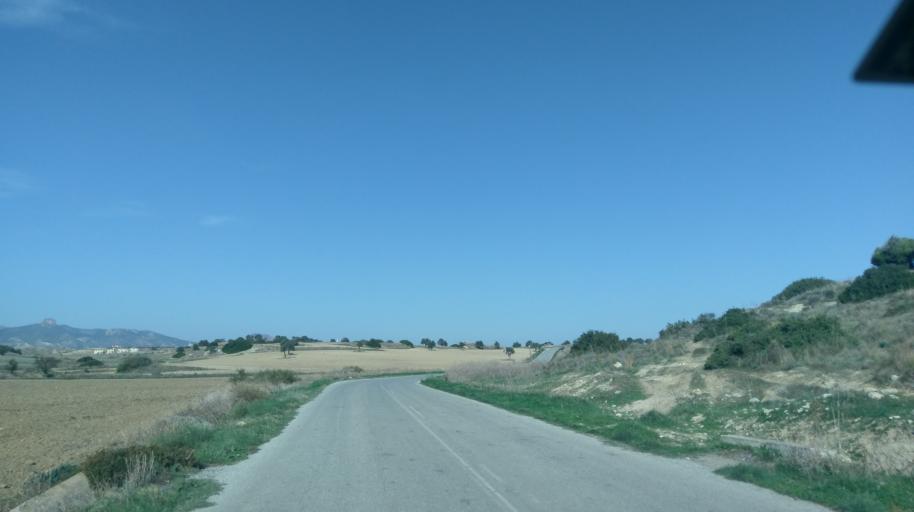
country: CY
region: Ammochostos
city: Trikomo
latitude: 35.3395
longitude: 33.9630
